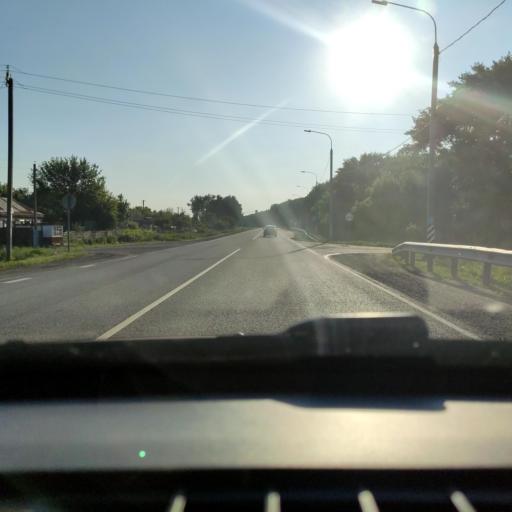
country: RU
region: Voronezj
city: Kashirskoye
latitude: 51.4587
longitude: 39.8012
